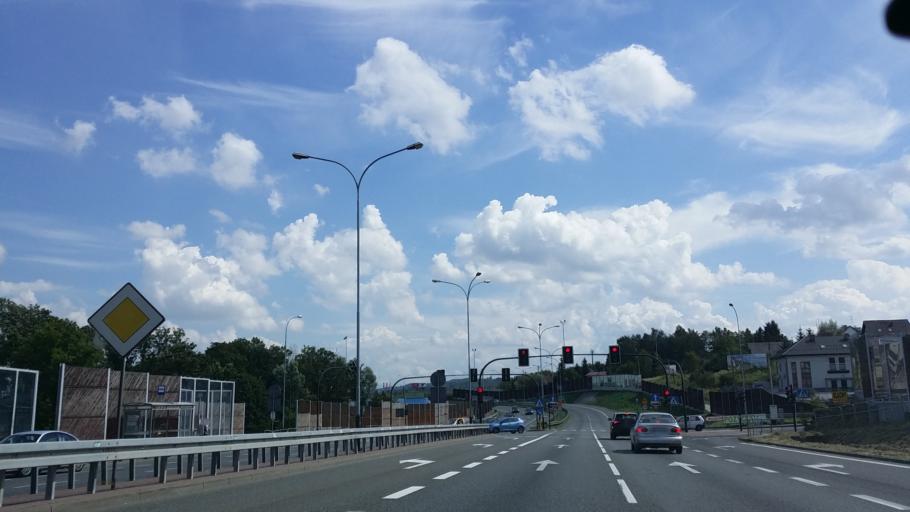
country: PL
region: Lesser Poland Voivodeship
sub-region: Powiat wielicki
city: Wieliczka
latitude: 50.0001
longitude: 20.0275
